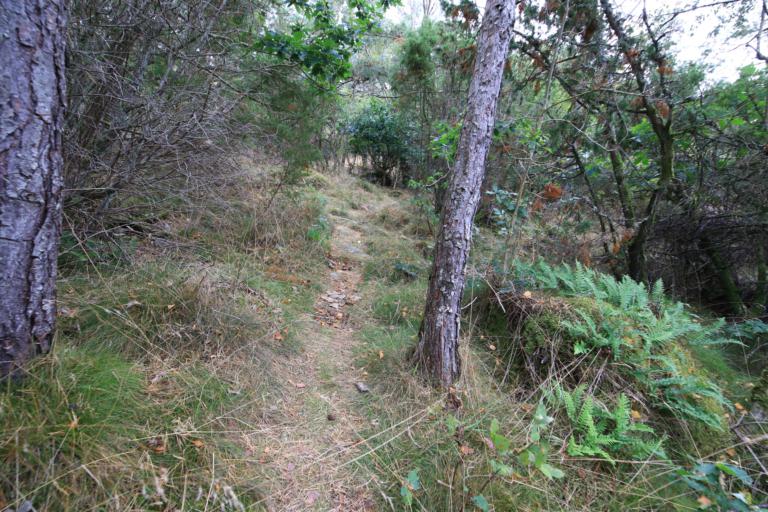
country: SE
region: Halland
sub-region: Varbergs Kommun
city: Varberg
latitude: 57.1752
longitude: 12.2060
